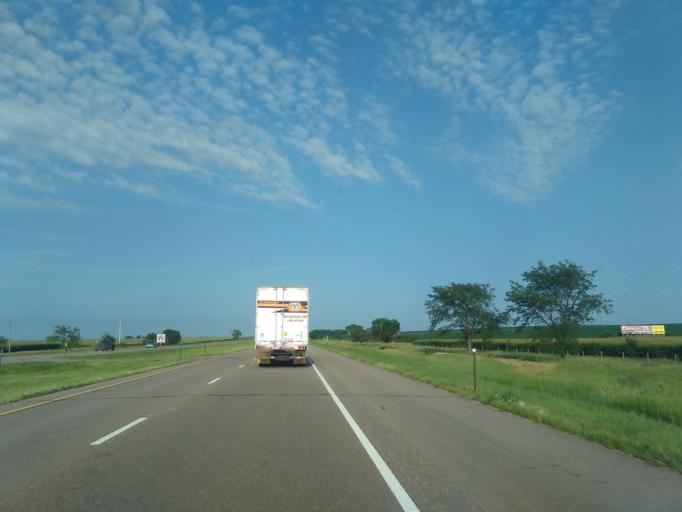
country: US
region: Nebraska
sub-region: York County
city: York
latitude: 40.8211
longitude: -97.6581
